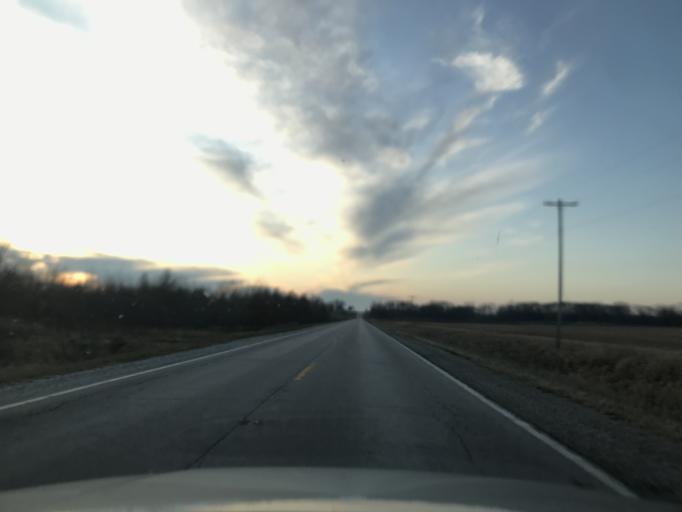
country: US
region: Illinois
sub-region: Henderson County
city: Oquawka
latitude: 41.0191
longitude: -90.8184
